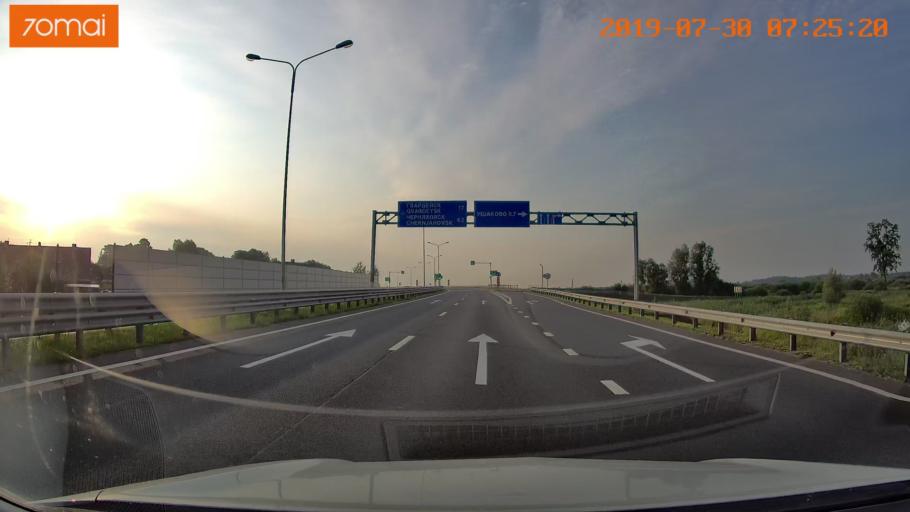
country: RU
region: Kaliningrad
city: Bol'shoe Isakovo
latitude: 54.6872
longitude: 20.8338
